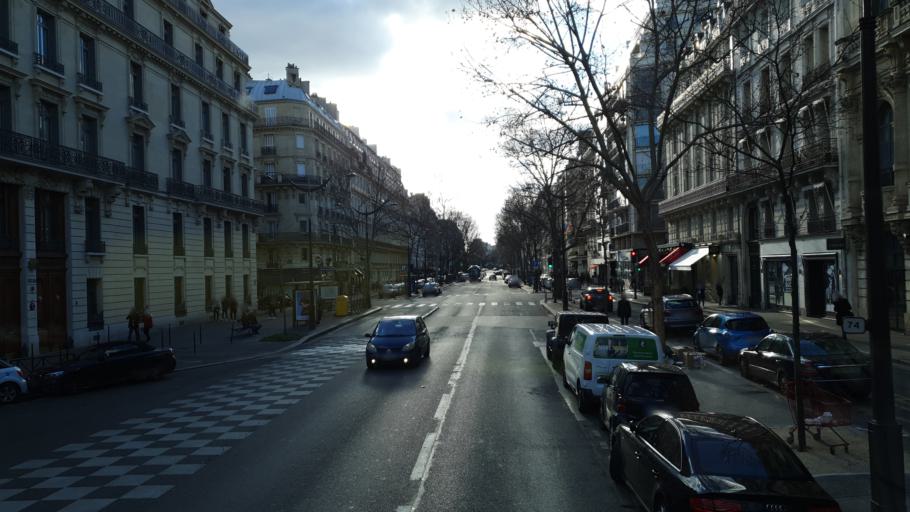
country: FR
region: Ile-de-France
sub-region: Departement des Hauts-de-Seine
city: Levallois-Perret
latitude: 48.8674
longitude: 2.2904
